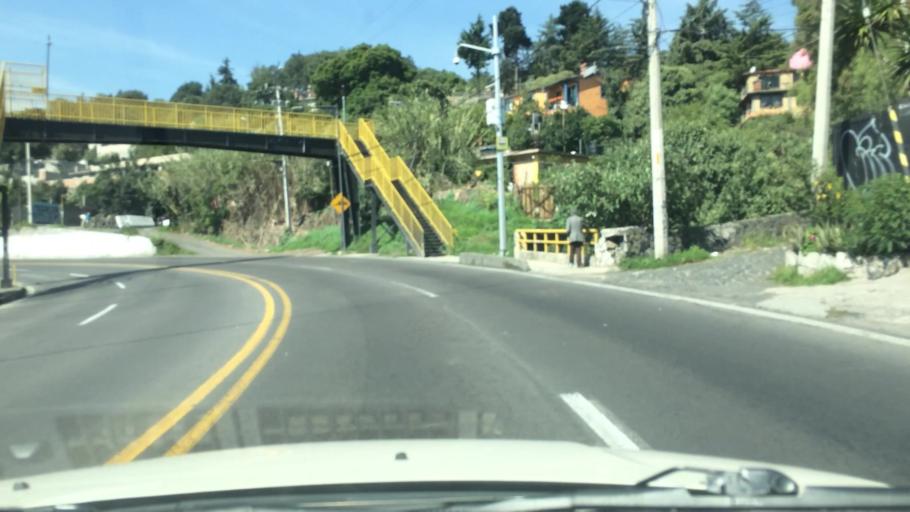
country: MX
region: Mexico City
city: Tlalpan
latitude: 19.2525
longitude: -99.1768
